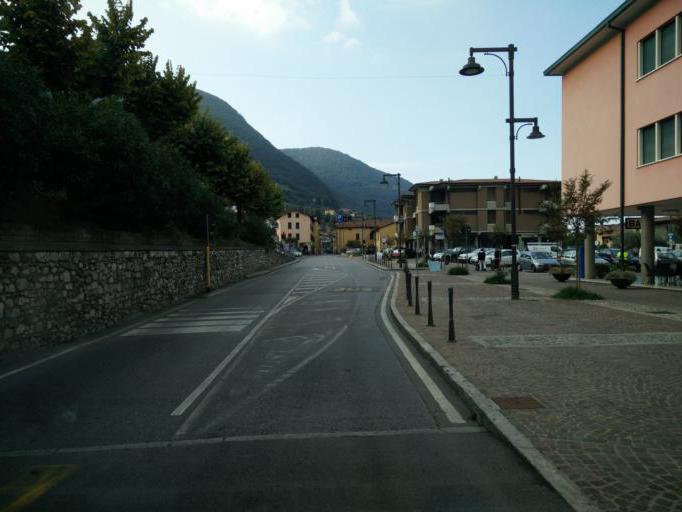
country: IT
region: Lombardy
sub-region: Provincia di Brescia
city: Sulzano
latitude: 45.6904
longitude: 10.1004
